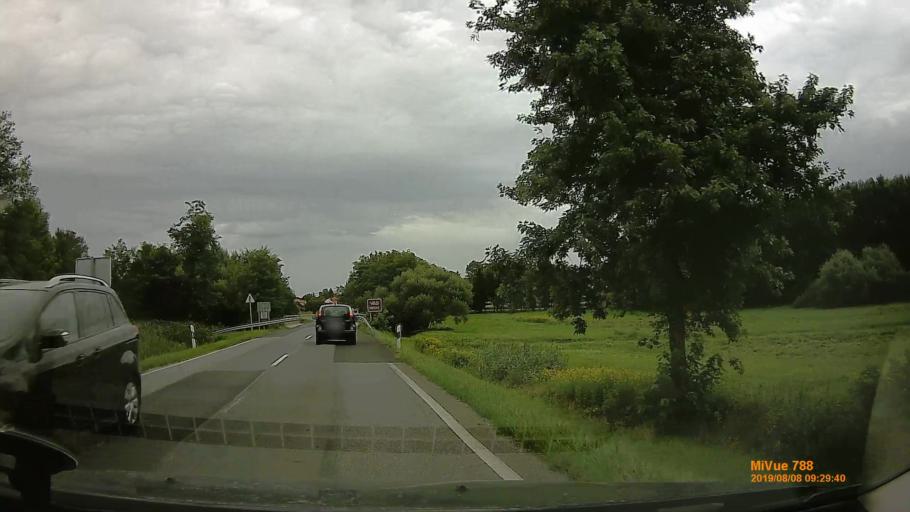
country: HU
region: Vas
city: Vasvar
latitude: 46.9779
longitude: 16.8420
